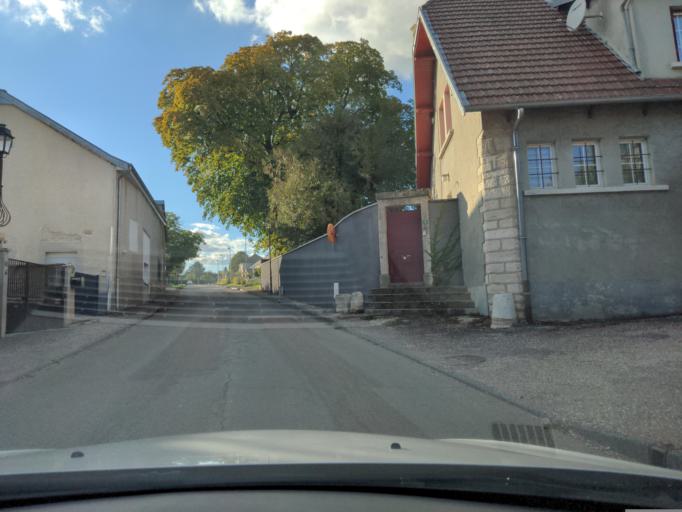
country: FR
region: Bourgogne
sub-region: Departement de la Cote-d'Or
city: Ruffey-les-Echirey
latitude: 47.3805
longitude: 5.0675
